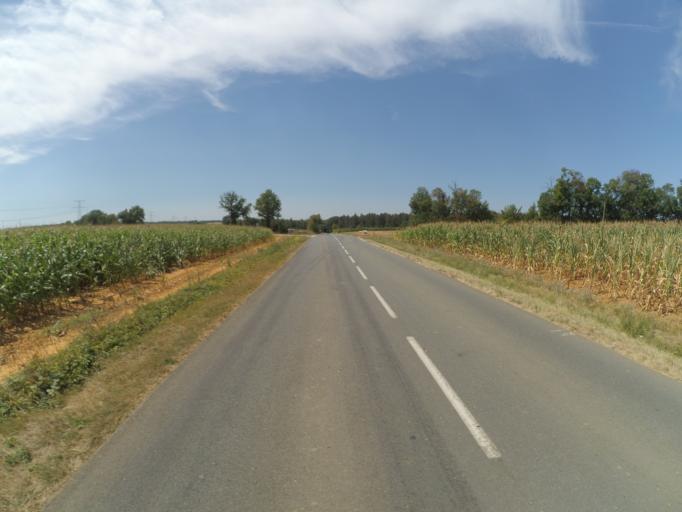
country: FR
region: Poitou-Charentes
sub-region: Departement de la Vienne
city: Saint-Maurice-la-Clouere
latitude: 46.3976
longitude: 0.3588
